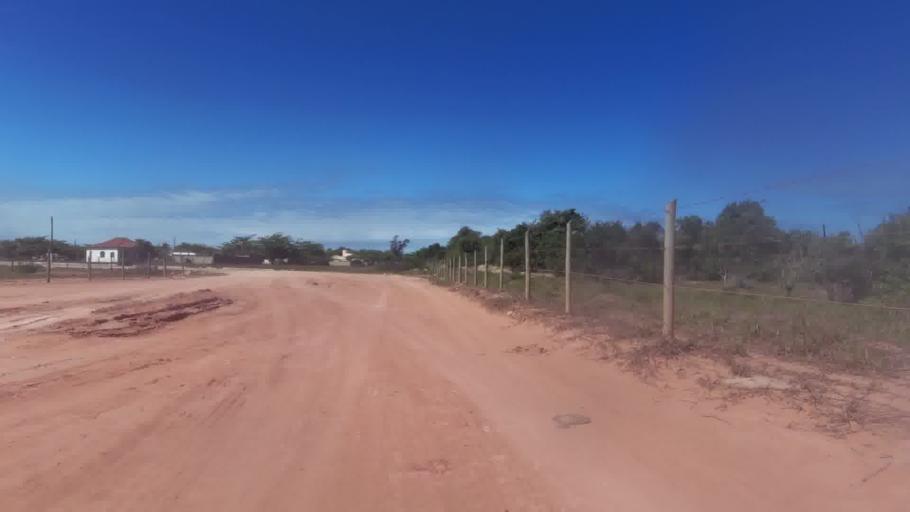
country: BR
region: Espirito Santo
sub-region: Marataizes
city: Marataizes
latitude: -21.1980
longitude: -40.9381
